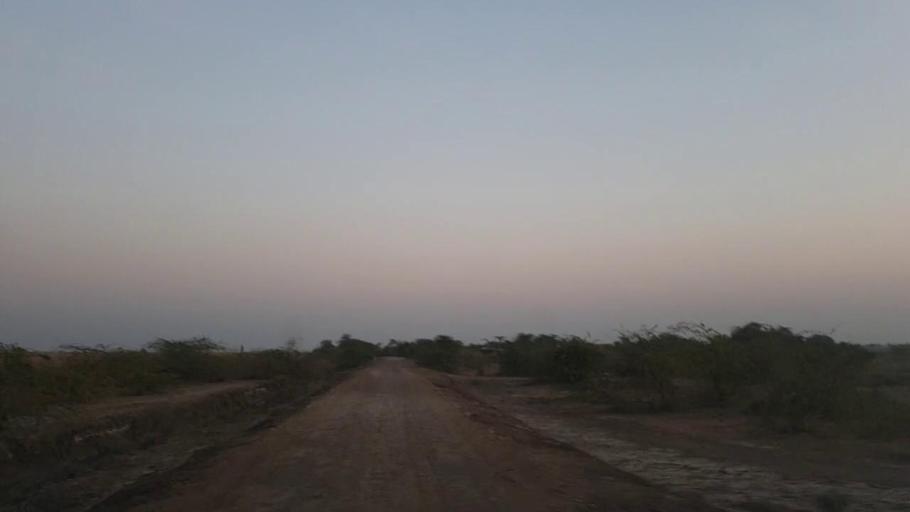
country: PK
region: Sindh
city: Naukot
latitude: 24.9947
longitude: 69.4380
